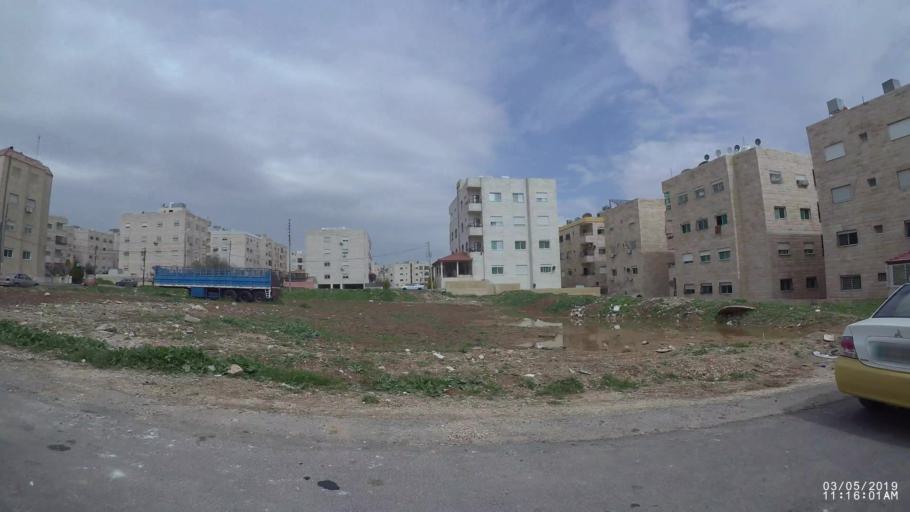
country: JO
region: Amman
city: Amman
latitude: 31.9883
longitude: 35.9275
